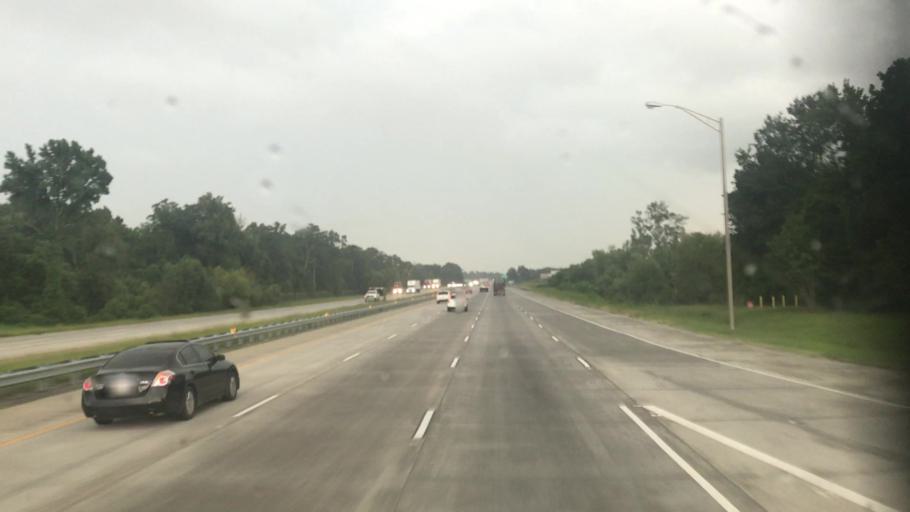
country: US
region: Georgia
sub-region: Dooly County
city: Unadilla
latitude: 32.2083
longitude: -83.7462
